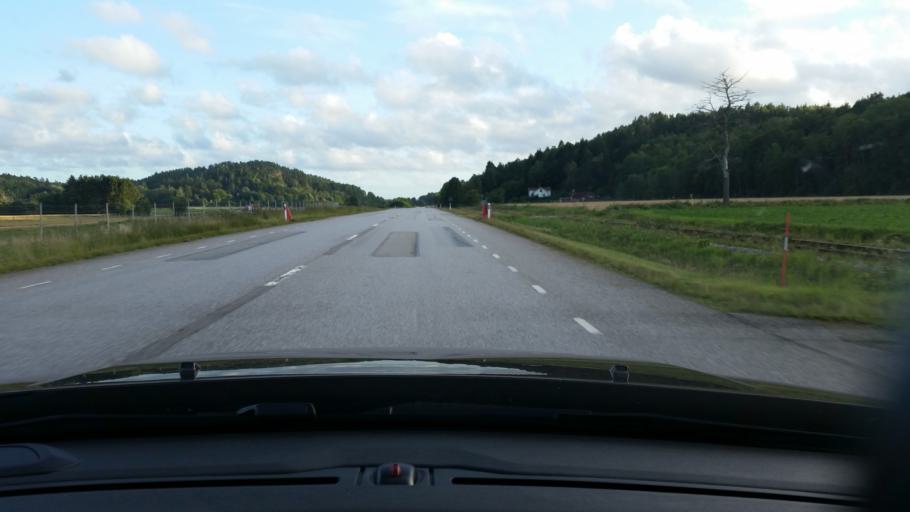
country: SE
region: Vaestra Goetaland
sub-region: Lilla Edets Kommun
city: Lodose
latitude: 58.0783
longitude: 12.1545
